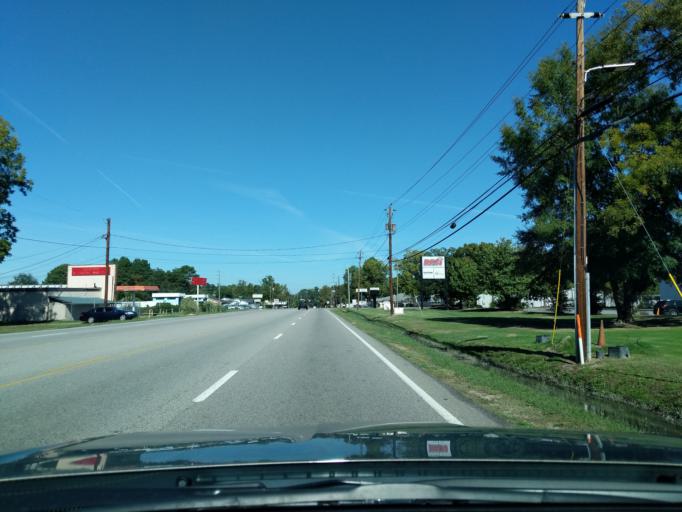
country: US
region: Georgia
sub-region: Richmond County
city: Augusta
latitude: 33.4134
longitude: -82.0067
